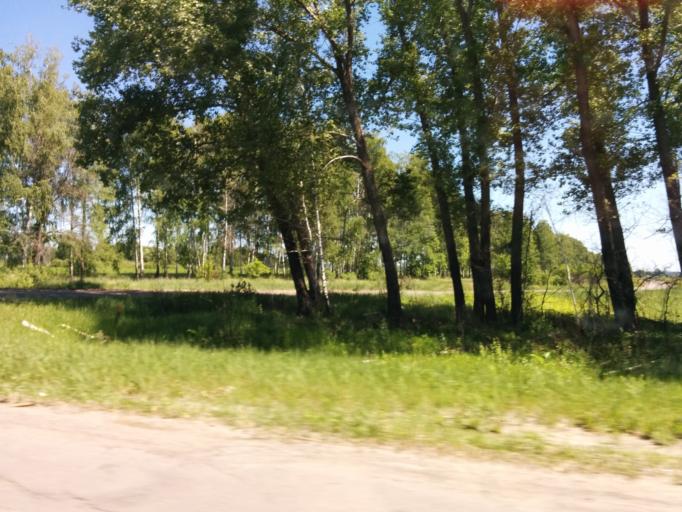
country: RU
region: Tambov
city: Goreloye
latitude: 53.0031
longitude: 41.4633
